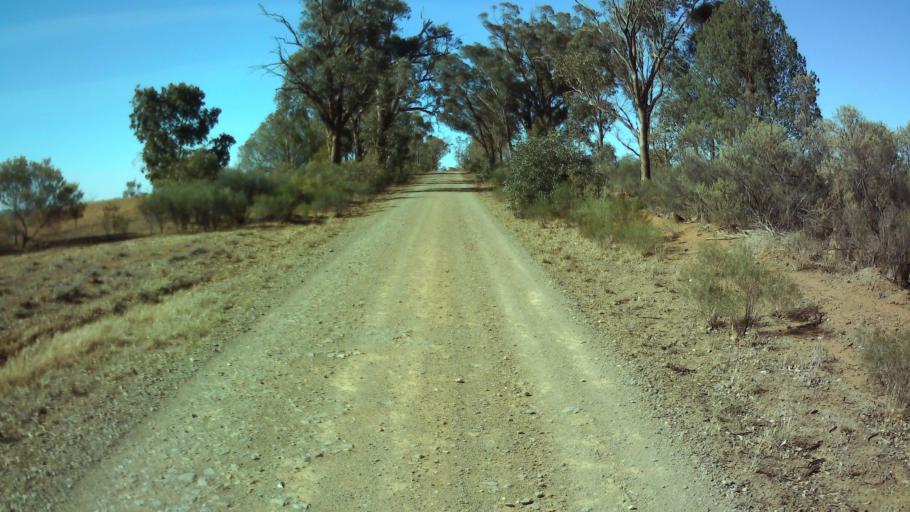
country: AU
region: New South Wales
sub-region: Weddin
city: Grenfell
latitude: -33.7489
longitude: 147.8303
